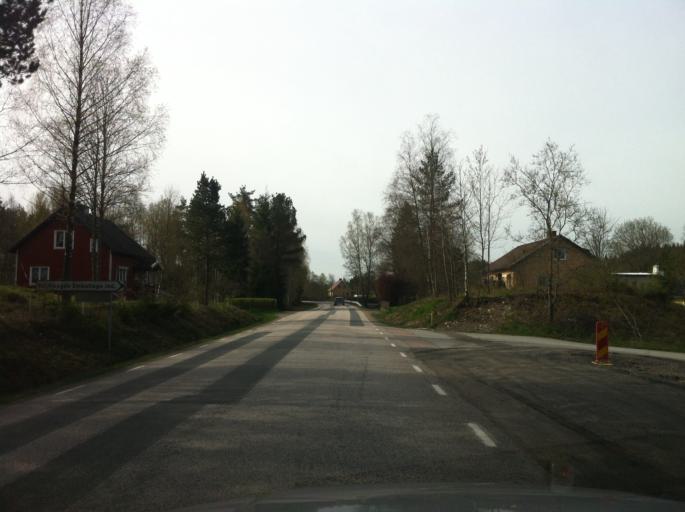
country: SE
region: Vaestra Goetaland
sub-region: Bollebygds Kommun
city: Bollebygd
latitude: 57.7328
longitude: 12.5904
